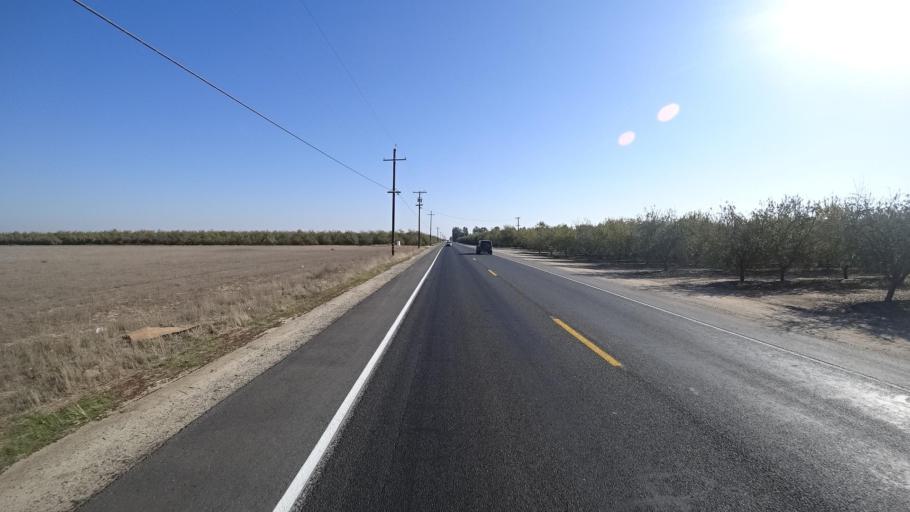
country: US
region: California
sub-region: Kern County
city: Delano
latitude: 35.7178
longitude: -119.3264
